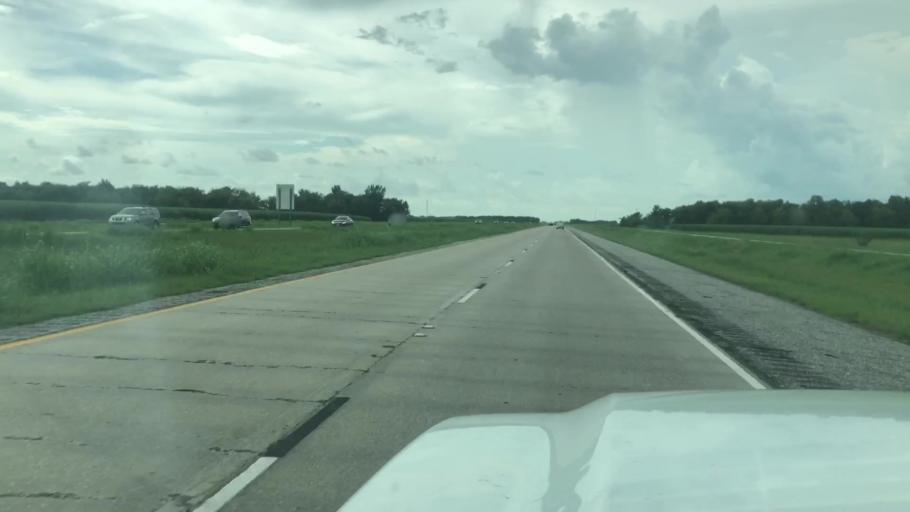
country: US
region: Louisiana
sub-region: Saint Mary Parish
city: Baldwin
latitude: 29.8454
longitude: -91.5853
